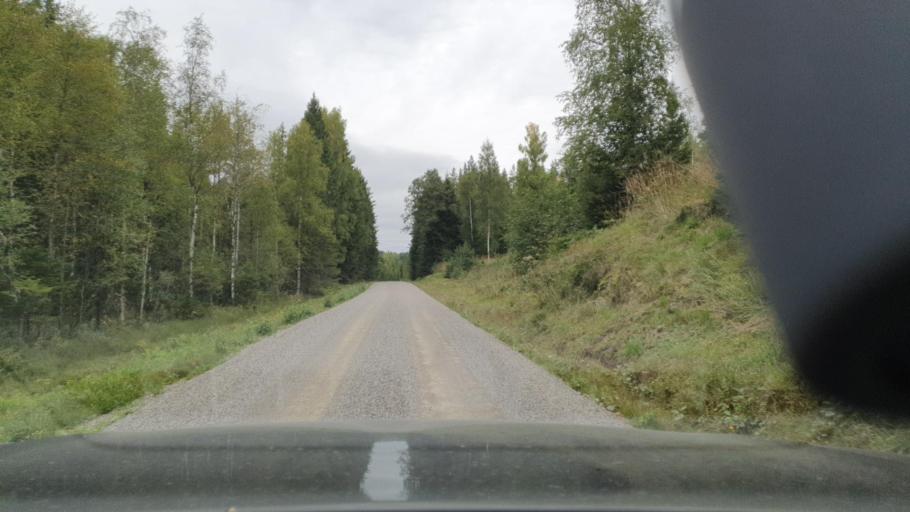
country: SE
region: Vaermland
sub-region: Eda Kommun
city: Charlottenberg
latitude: 60.0524
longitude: 12.6295
